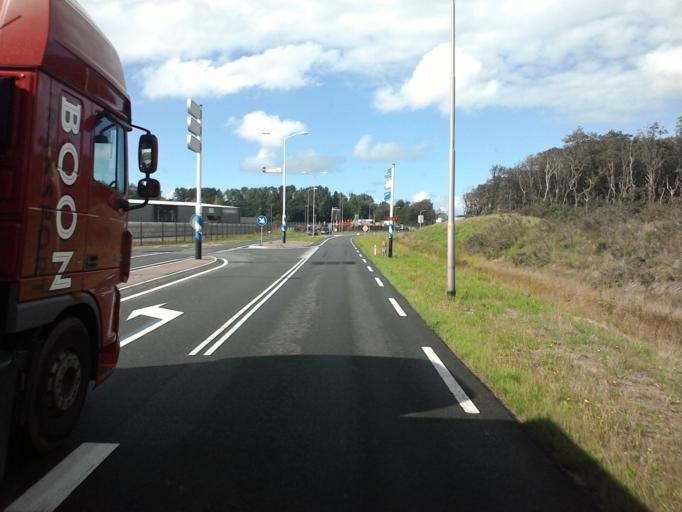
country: NL
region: North Holland
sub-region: Gemeente Beverwijk
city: Beverwijk
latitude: 52.4847
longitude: 4.6301
